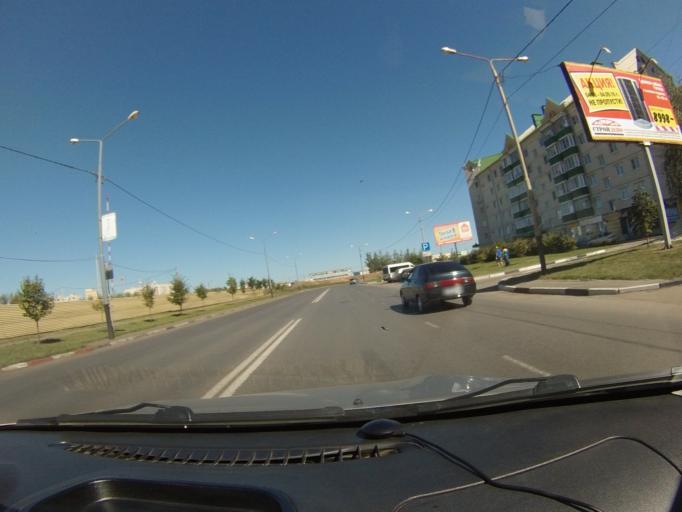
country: RU
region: Tambov
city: Tambov
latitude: 52.7712
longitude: 41.4099
